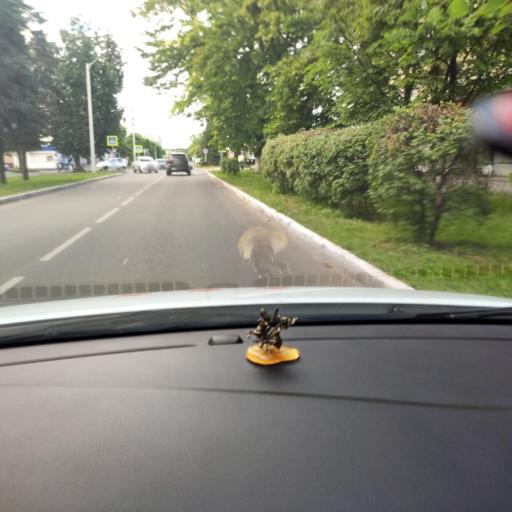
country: RU
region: Tatarstan
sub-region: Zelenodol'skiy Rayon
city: Zelenodolsk
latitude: 55.8483
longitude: 48.4982
